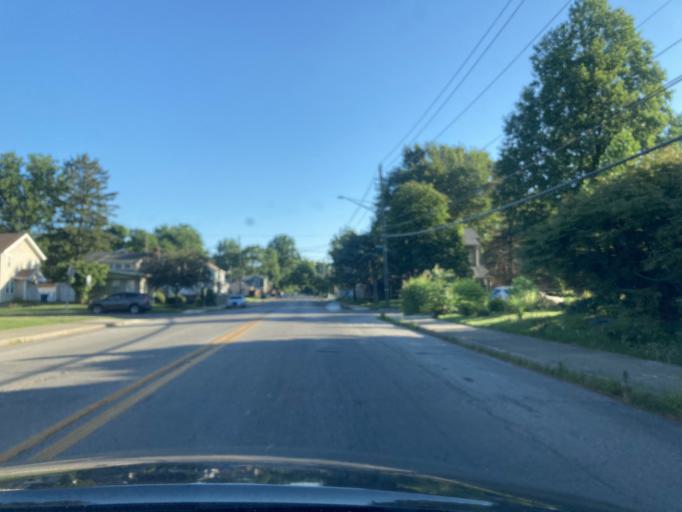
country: US
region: Indiana
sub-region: Marion County
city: Broad Ripple
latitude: 39.8344
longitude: -86.1640
